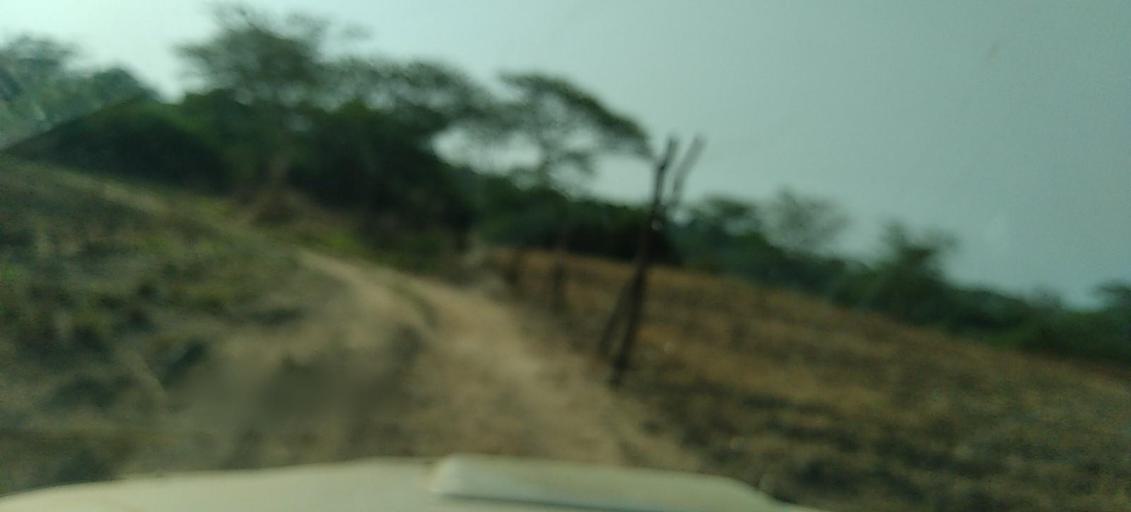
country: ZM
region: North-Western
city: Kasempa
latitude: -13.1905
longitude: 25.9700
